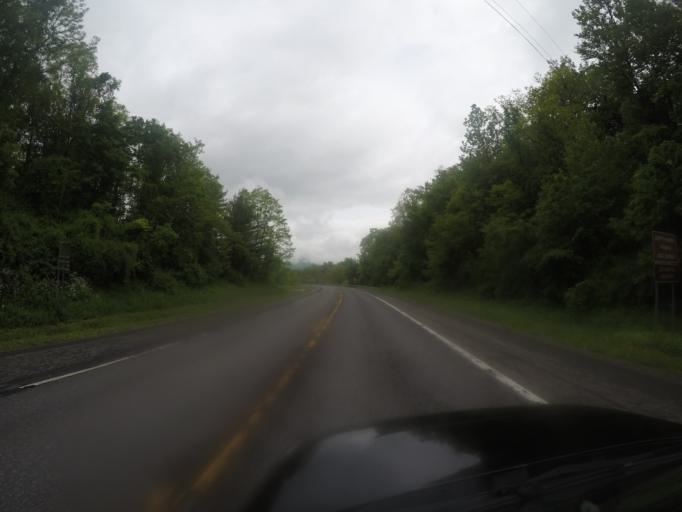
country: US
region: New York
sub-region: Ulster County
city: Shokan
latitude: 42.0213
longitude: -74.2693
